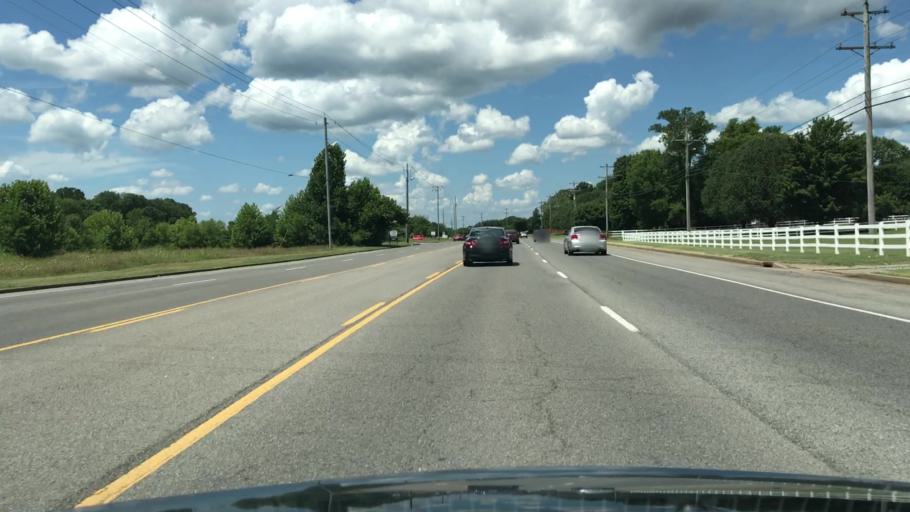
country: US
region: Tennessee
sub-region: Rutherford County
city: Murfreesboro
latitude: 35.8442
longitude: -86.4642
